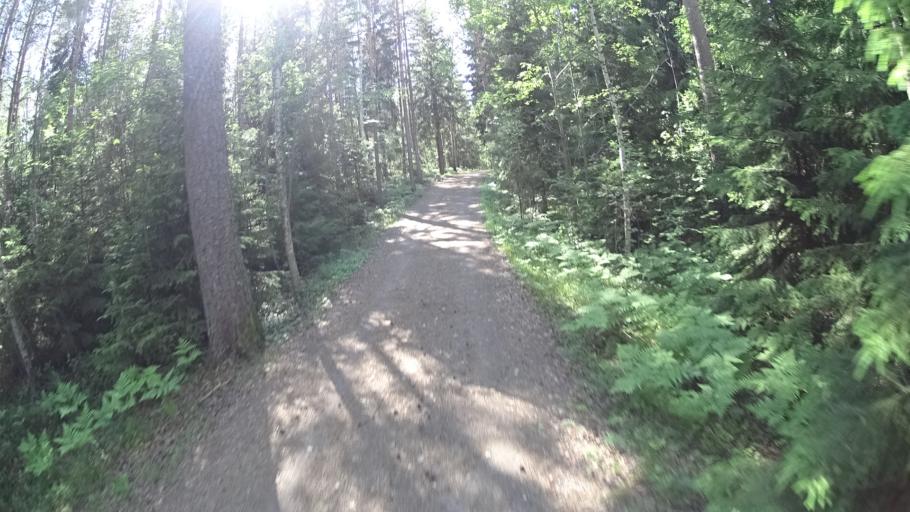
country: FI
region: Uusimaa
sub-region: Helsinki
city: Vantaa
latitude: 60.2350
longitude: 25.1803
